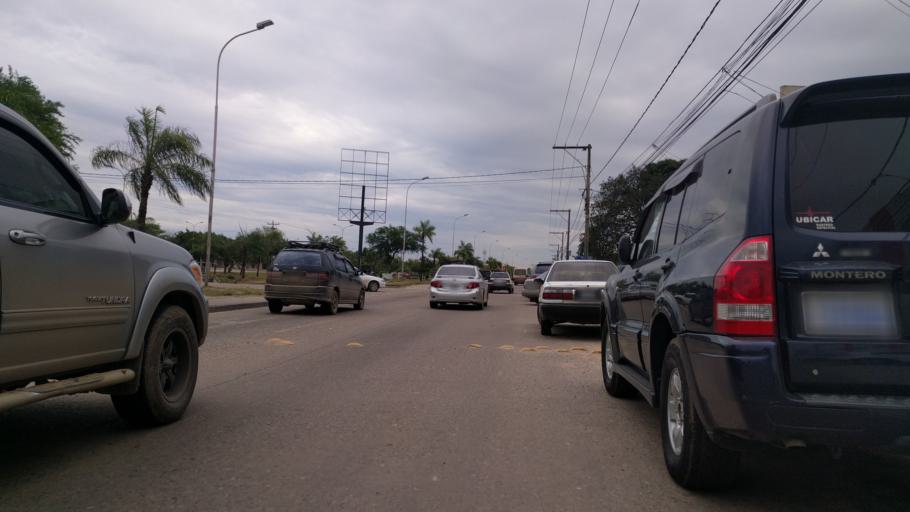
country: BO
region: Santa Cruz
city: Santa Cruz de la Sierra
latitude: -17.8208
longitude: -63.1940
